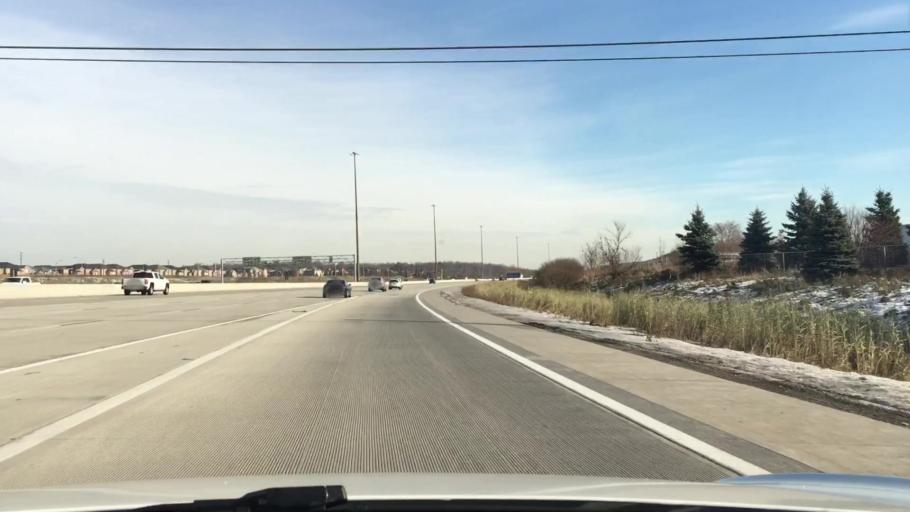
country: CA
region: Ontario
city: Concord
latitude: 43.8204
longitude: -79.4738
